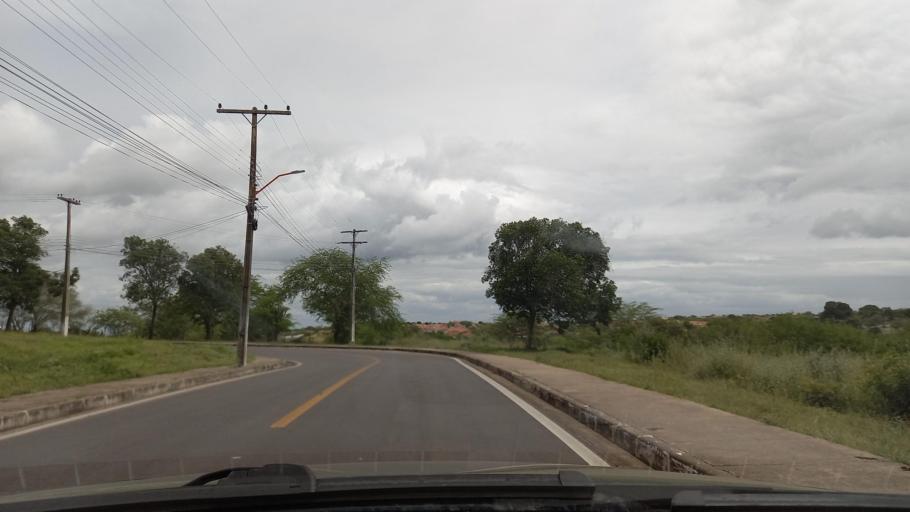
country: BR
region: Sergipe
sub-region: Caninde De Sao Francisco
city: Caninde de Sao Francisco
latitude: -9.6077
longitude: -37.7670
